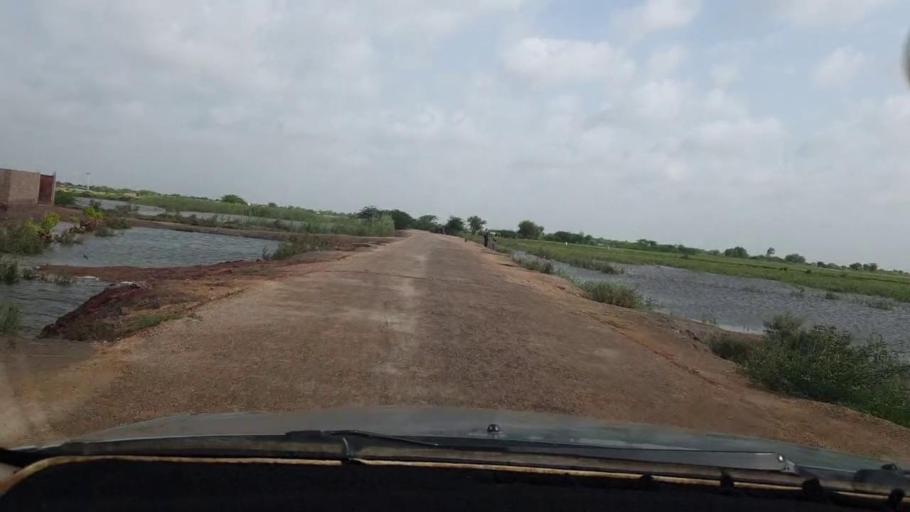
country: PK
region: Sindh
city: Tando Bago
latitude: 24.7886
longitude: 68.9799
